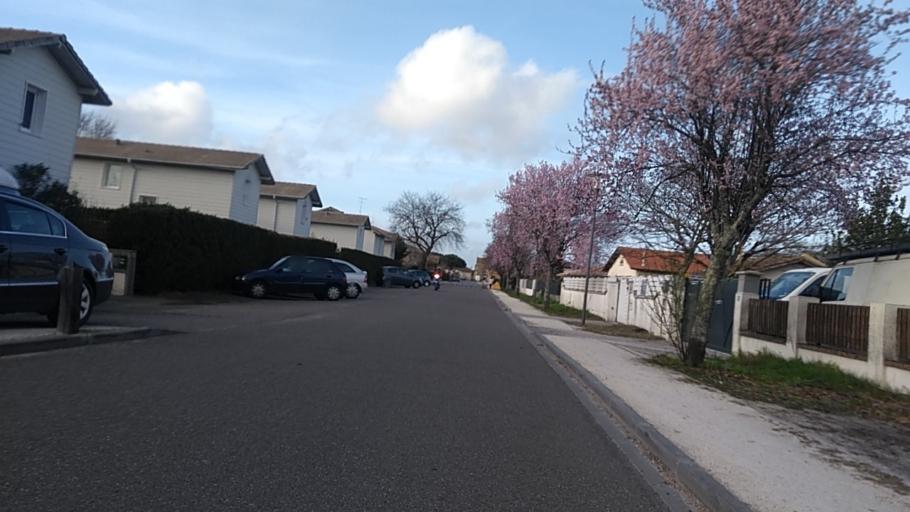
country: FR
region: Aquitaine
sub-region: Departement de la Gironde
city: Le Barp
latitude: 44.6027
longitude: -0.7689
